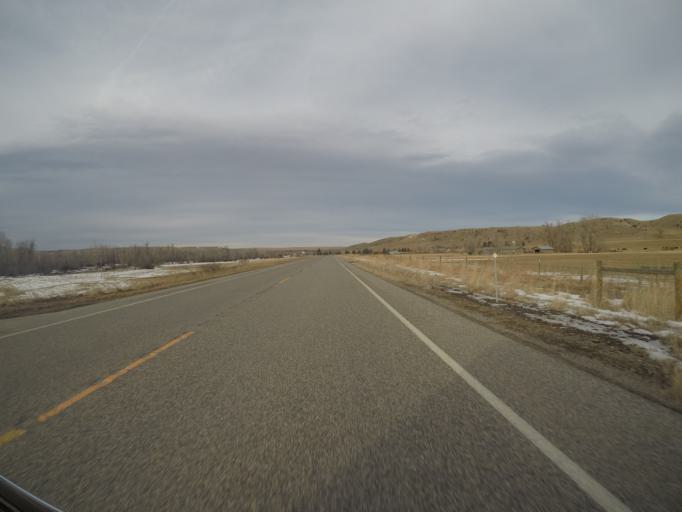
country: US
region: Montana
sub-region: Stillwater County
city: Absarokee
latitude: 45.4740
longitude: -109.4486
